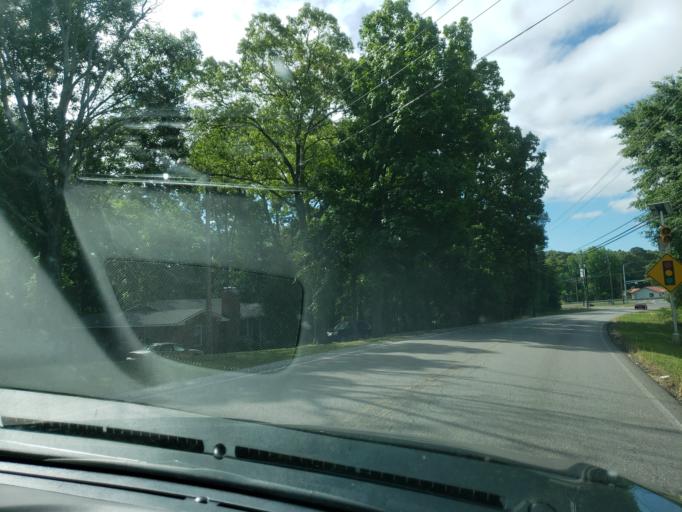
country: US
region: Alabama
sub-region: Calhoun County
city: Saks
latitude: 33.7241
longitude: -85.8441
